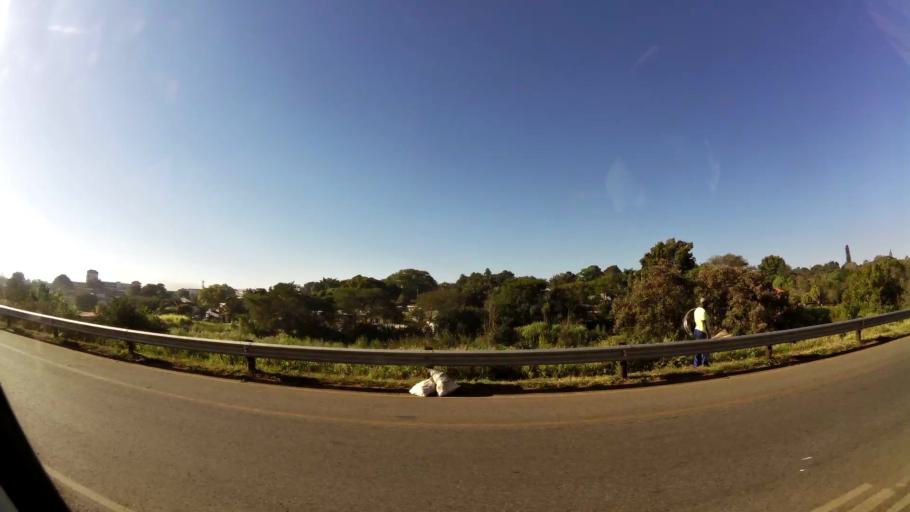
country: ZA
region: Limpopo
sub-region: Mopani District Municipality
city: Tzaneen
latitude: -23.8264
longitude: 30.1541
